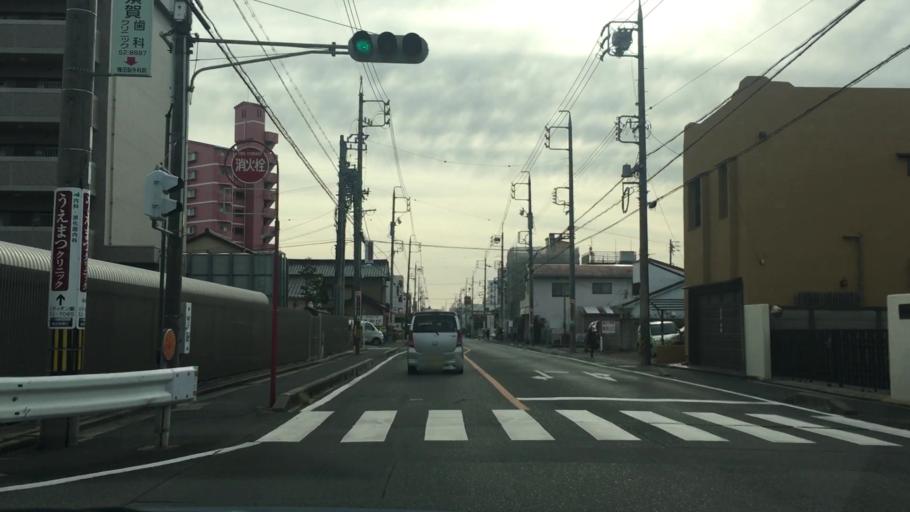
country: JP
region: Aichi
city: Toyohashi
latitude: 34.7573
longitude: 137.3950
